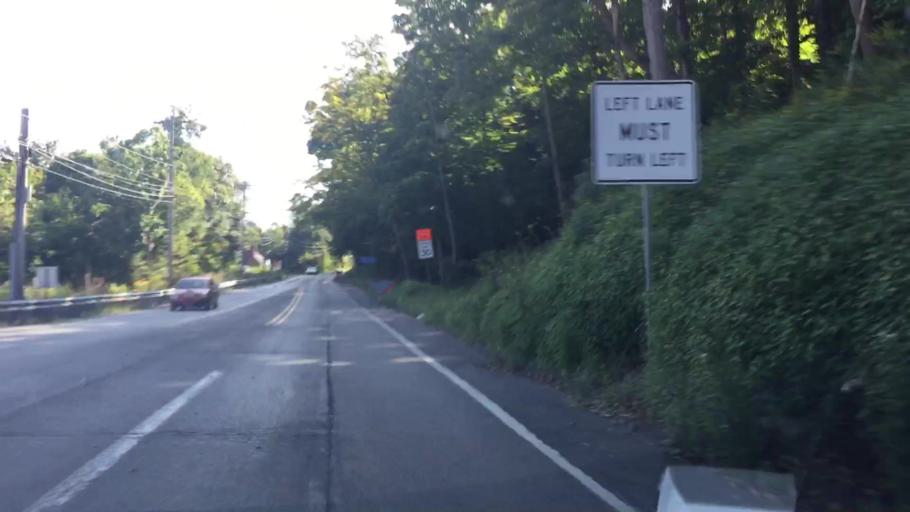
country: US
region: Pennsylvania
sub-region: Allegheny County
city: Franklin Park
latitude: 40.5531
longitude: -80.1142
